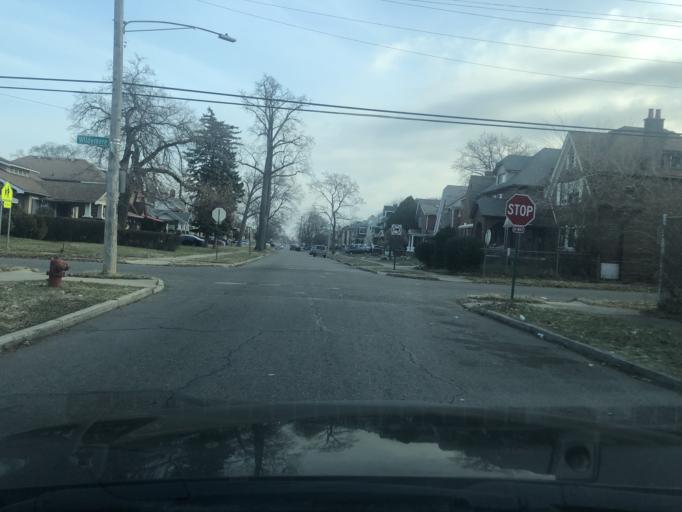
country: US
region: Michigan
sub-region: Wayne County
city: Highland Park
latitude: 42.3881
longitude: -83.1257
